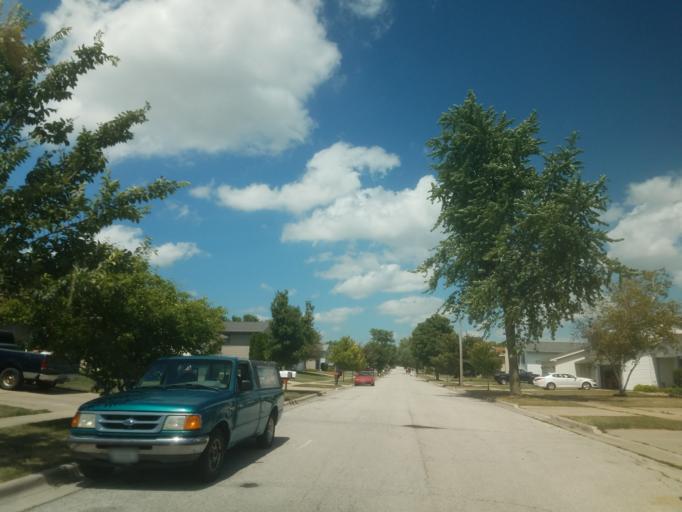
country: US
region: Illinois
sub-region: McLean County
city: Bloomington
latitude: 40.4416
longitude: -89.0312
